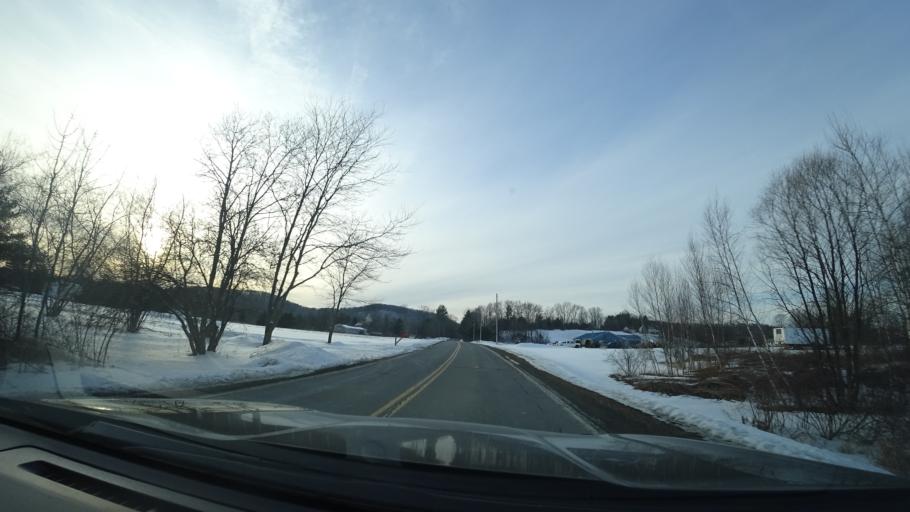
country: US
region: New York
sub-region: Washington County
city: Cambridge
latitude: 43.1725
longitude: -73.3541
